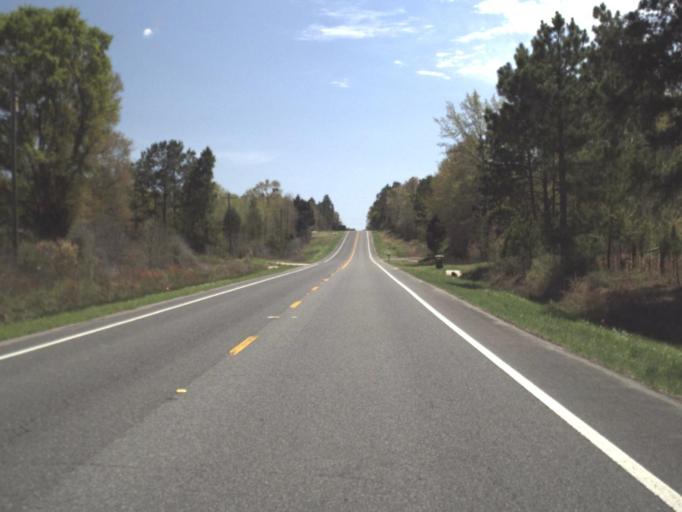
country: US
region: Alabama
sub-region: Geneva County
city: Geneva
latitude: 30.8766
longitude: -85.9481
